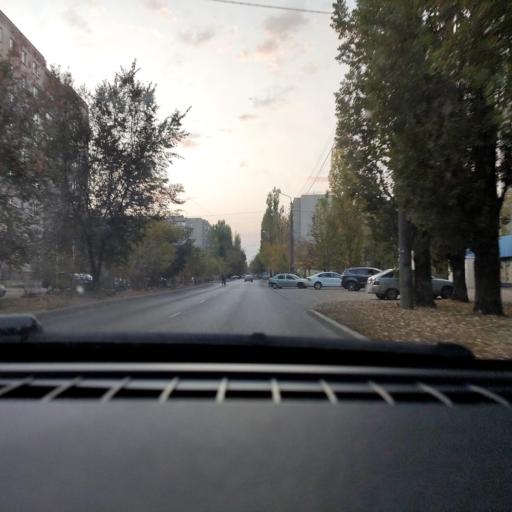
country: RU
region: Voronezj
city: Maslovka
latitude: 51.6329
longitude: 39.2839
